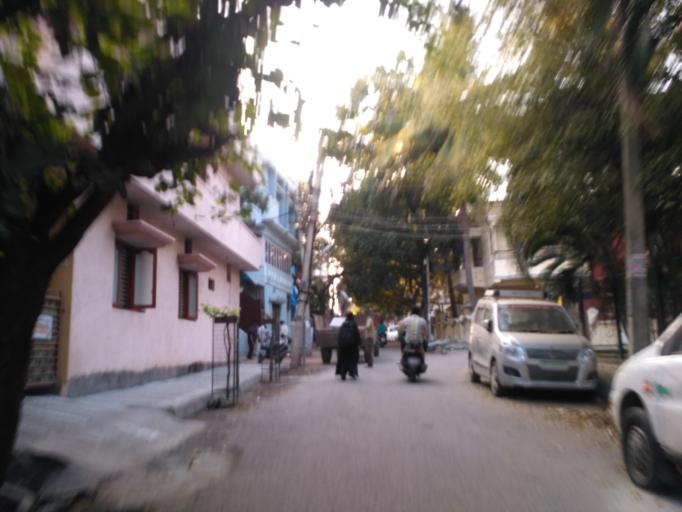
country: IN
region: Karnataka
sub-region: Bangalore Urban
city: Bangalore
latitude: 12.9580
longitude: 77.5311
